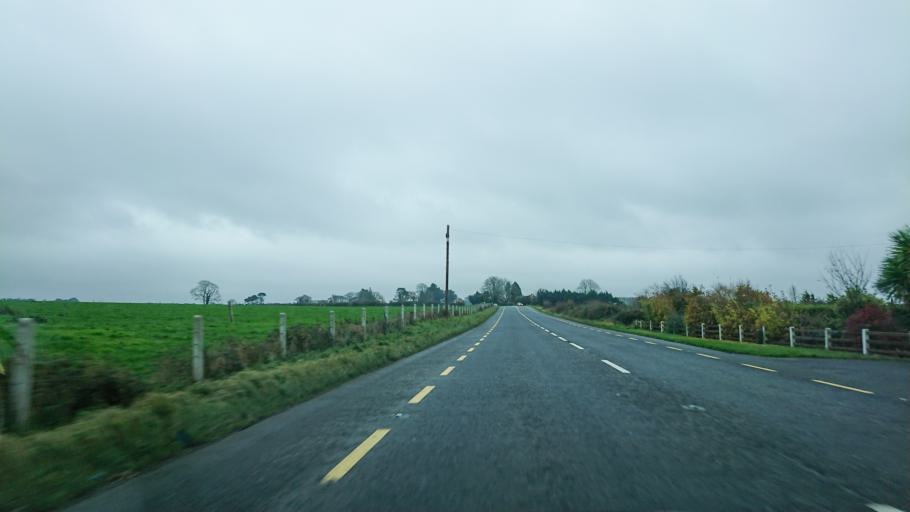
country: IE
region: Leinster
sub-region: Kilkenny
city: Mooncoin
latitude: 52.2840
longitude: -7.2107
